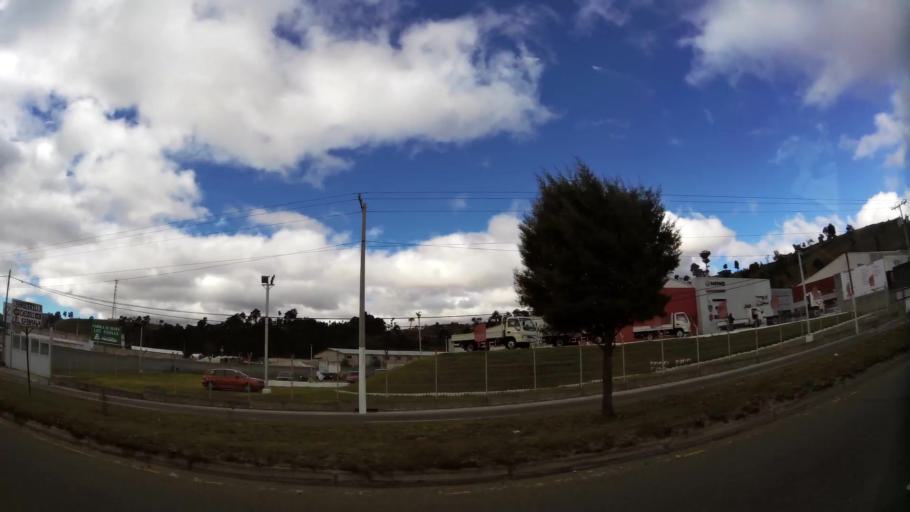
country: GT
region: Quetzaltenango
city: Salcaja
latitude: 14.8690
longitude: -91.4677
